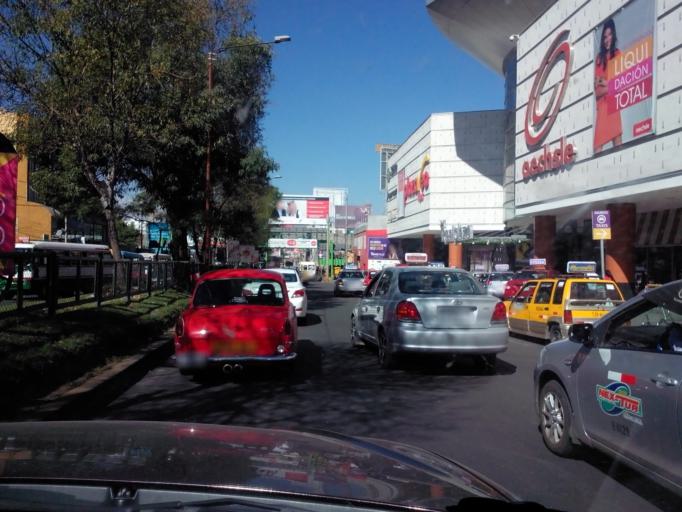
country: PE
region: Arequipa
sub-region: Provincia de Arequipa
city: Arequipa
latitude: -16.3890
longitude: -71.5497
